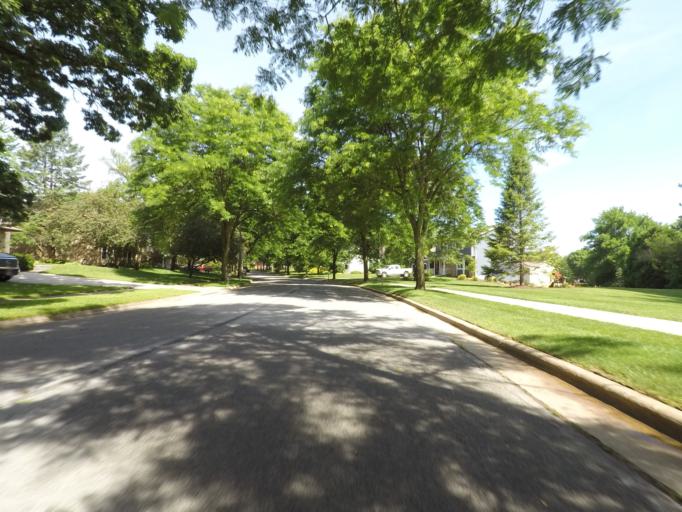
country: US
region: Wisconsin
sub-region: Dane County
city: Middleton
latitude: 43.0830
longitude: -89.5108
